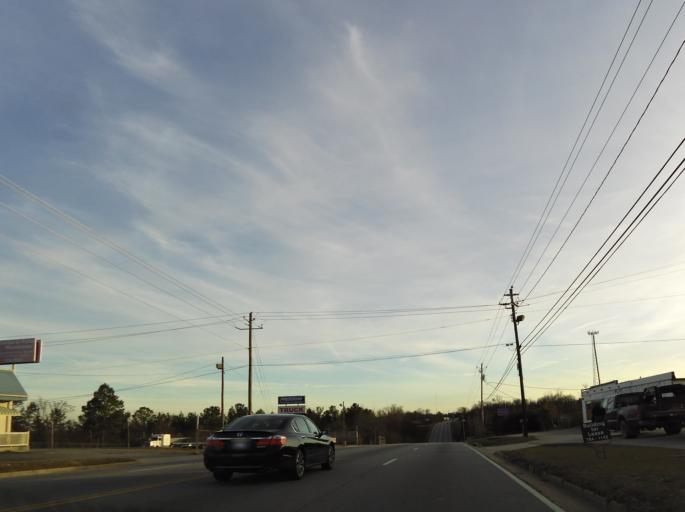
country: US
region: Georgia
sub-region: Bibb County
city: Macon
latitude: 32.8055
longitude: -83.6405
